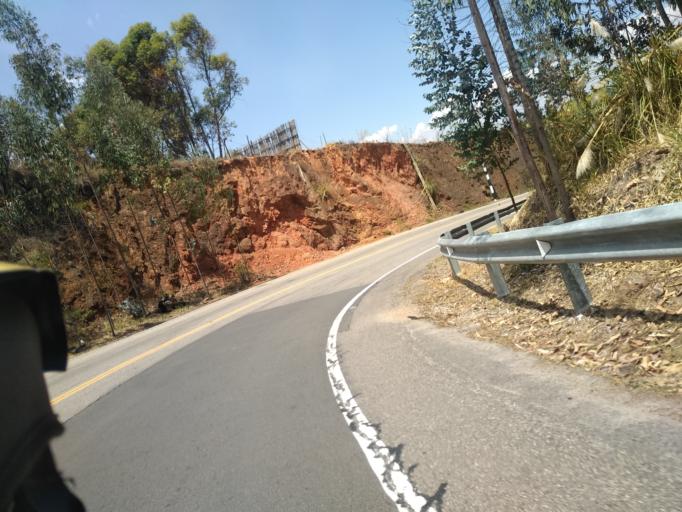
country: PE
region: Cajamarca
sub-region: San Marcos
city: San Marcos
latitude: -7.2866
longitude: -78.2062
